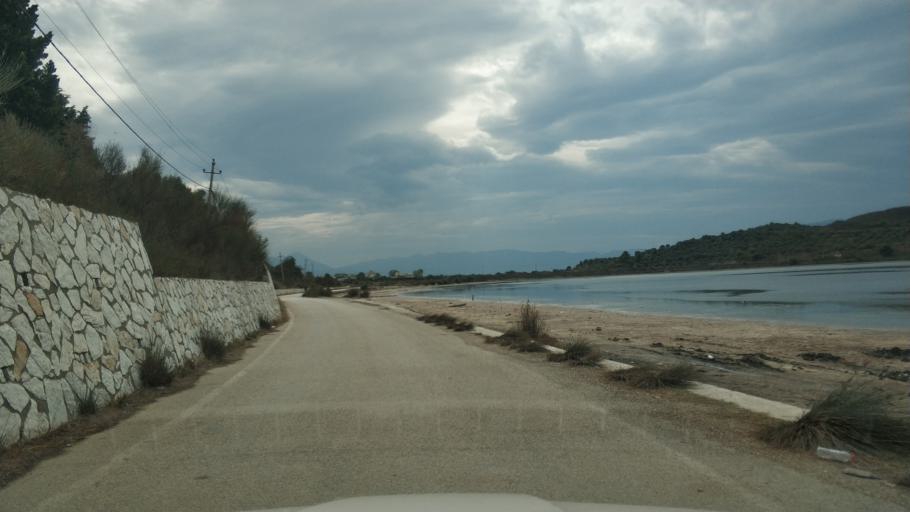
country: AL
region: Vlore
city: Vlore
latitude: 40.5168
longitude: 19.4066
